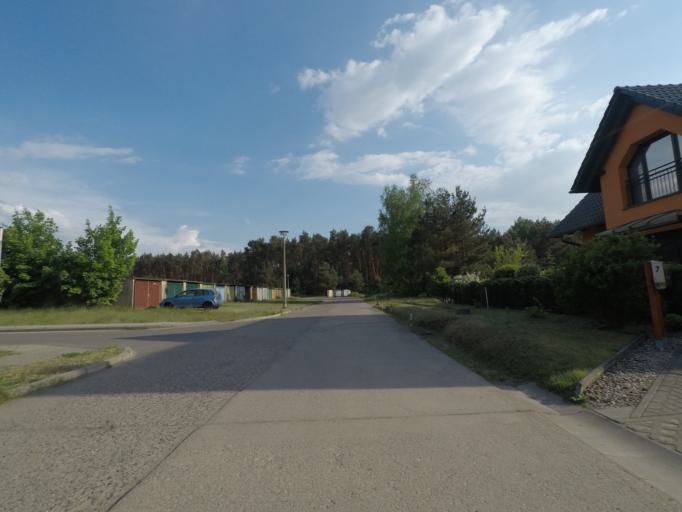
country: DE
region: Brandenburg
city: Melchow
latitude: 52.8321
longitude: 13.7317
